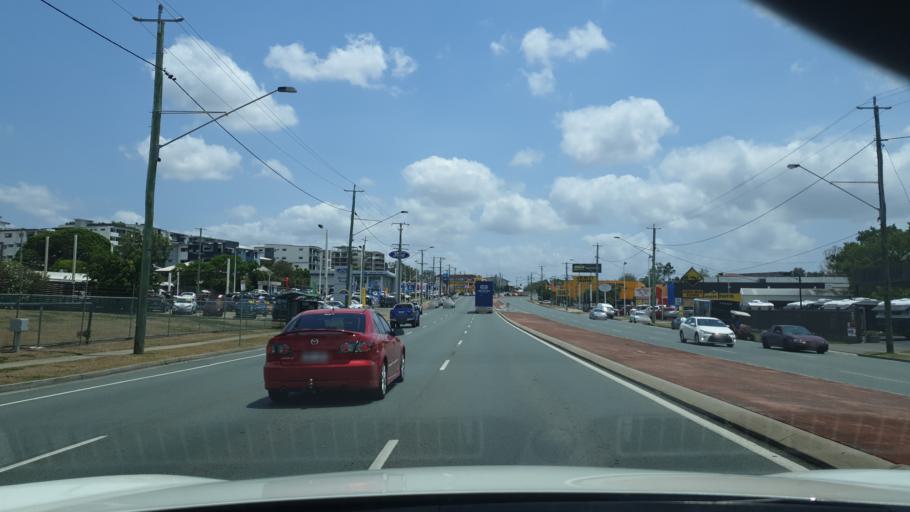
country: AU
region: Queensland
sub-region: Brisbane
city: Wavell Heights
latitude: -27.3975
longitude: 153.0312
